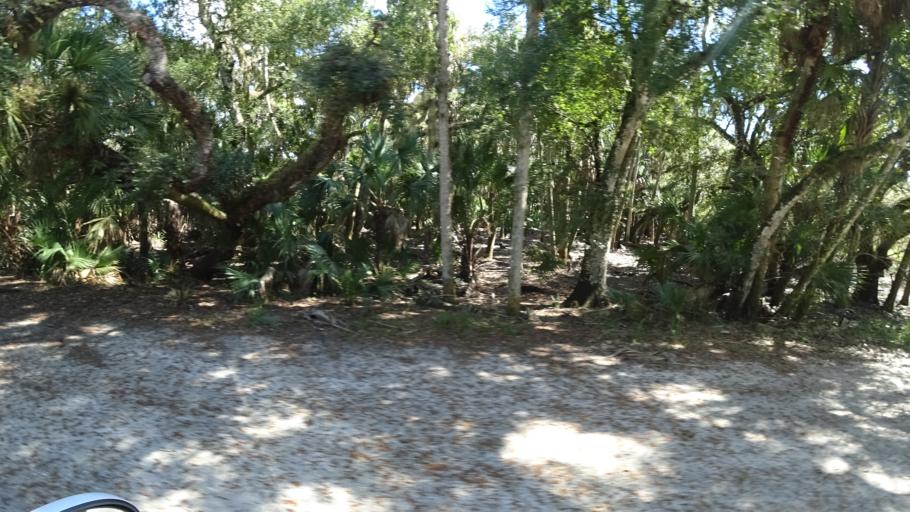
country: US
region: Florida
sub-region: Sarasota County
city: Lake Sarasota
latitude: 27.2511
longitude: -82.2941
